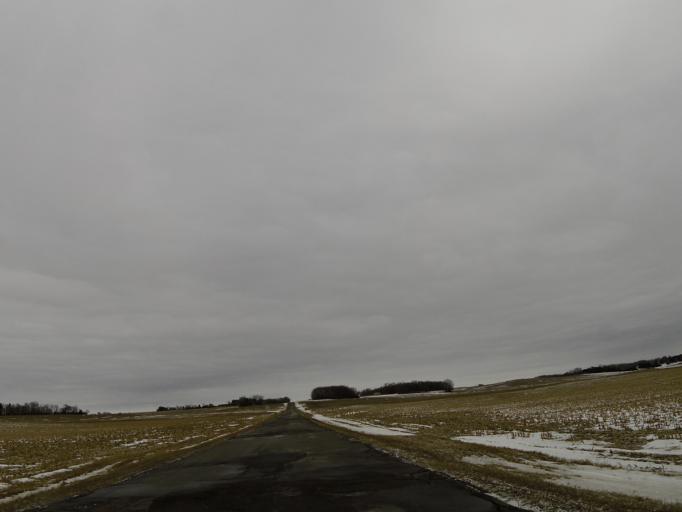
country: US
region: Minnesota
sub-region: Washington County
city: Cottage Grove
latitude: 44.8045
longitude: -92.8869
